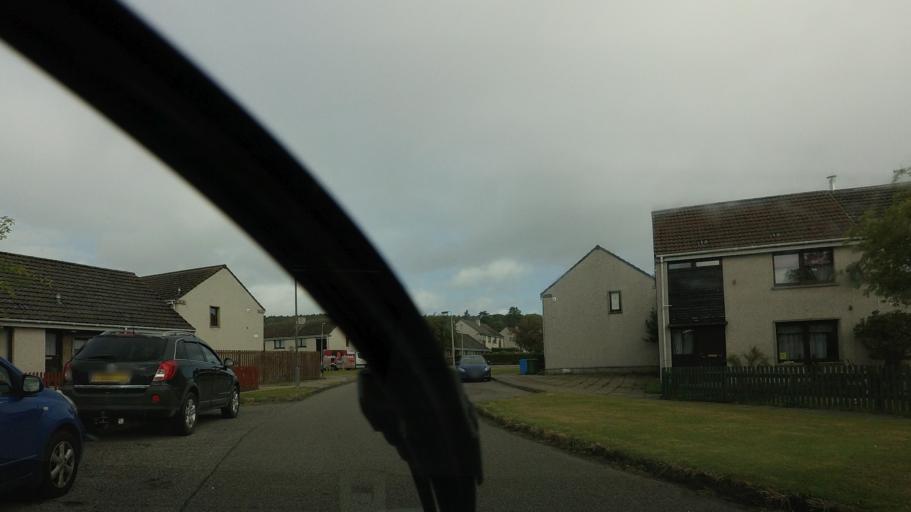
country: GB
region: Scotland
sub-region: Highland
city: Alness
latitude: 57.6943
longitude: -4.2713
